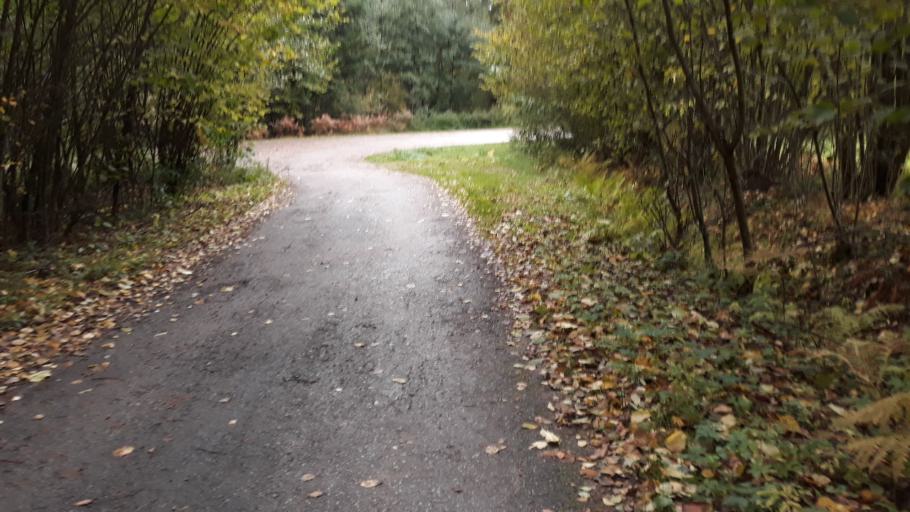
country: PL
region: Lublin Voivodeship
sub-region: Powiat janowski
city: Dzwola
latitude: 50.6791
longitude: 22.5502
